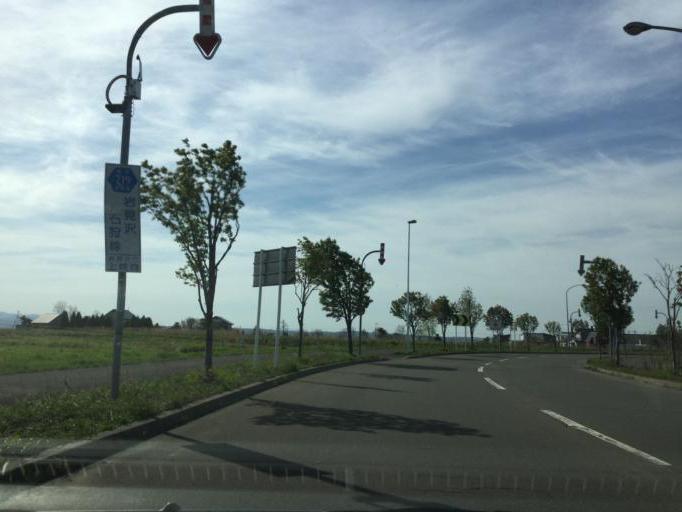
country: JP
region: Hokkaido
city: Iwamizawa
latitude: 43.1769
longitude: 141.7109
